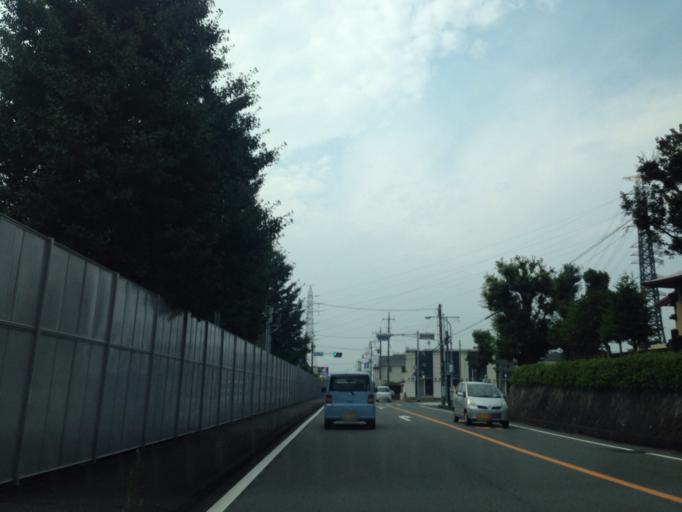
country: JP
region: Shizuoka
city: Mishima
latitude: 35.1602
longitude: 138.9075
